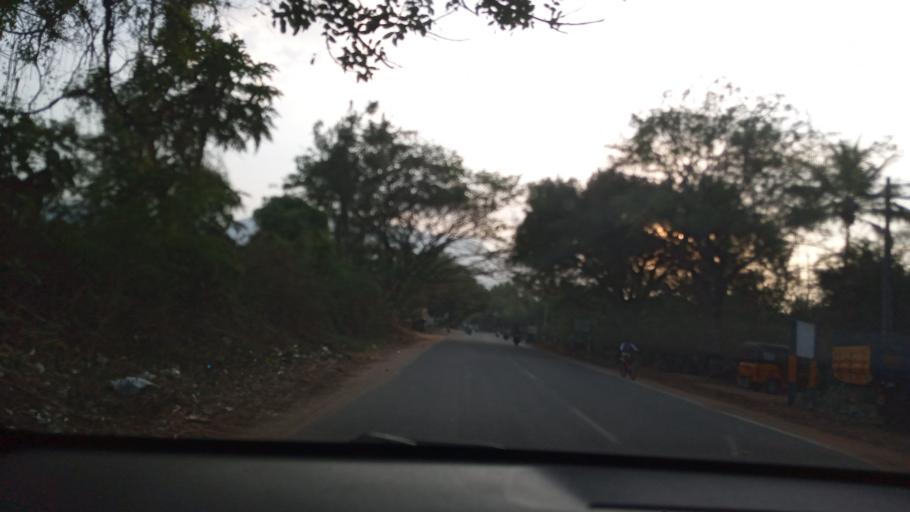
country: IN
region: Tamil Nadu
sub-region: Coimbatore
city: Perur
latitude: 10.9475
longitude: 76.7774
